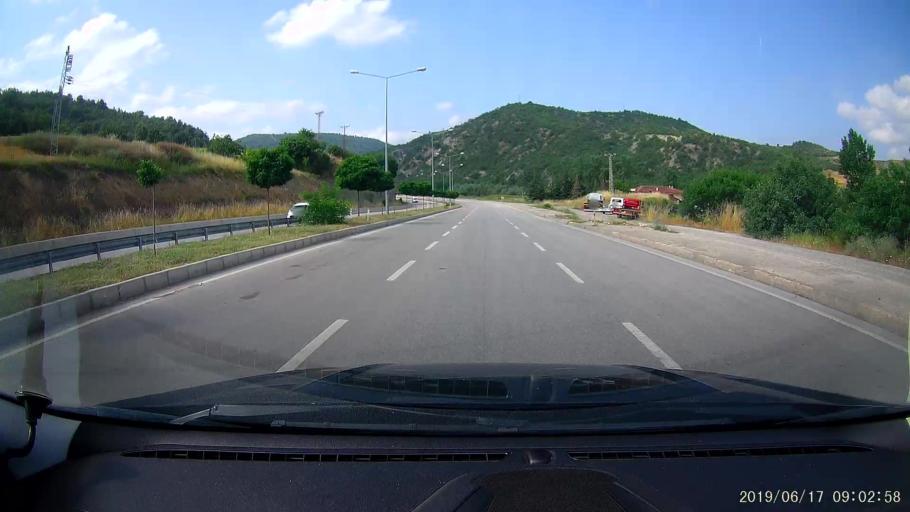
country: TR
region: Amasya
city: Tasova
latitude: 40.7609
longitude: 36.3039
